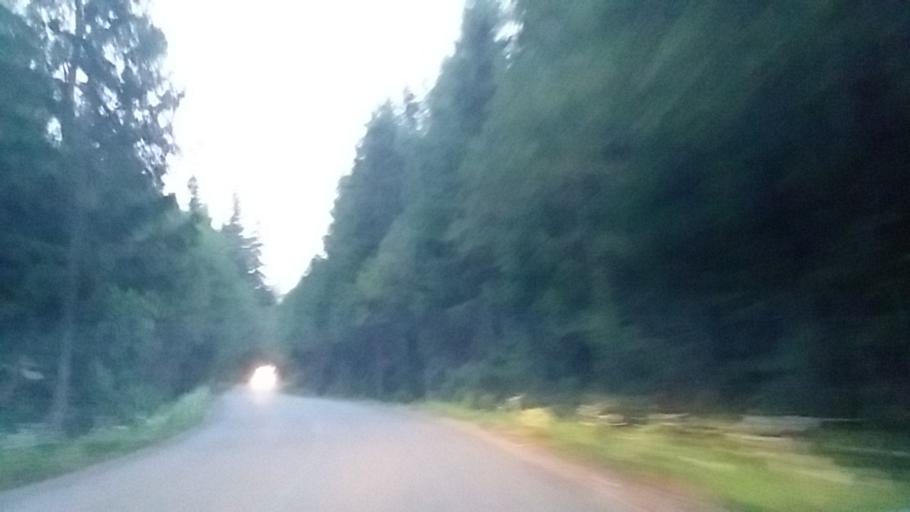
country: US
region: Washington
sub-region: Kittitas County
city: Cle Elum
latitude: 47.3544
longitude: -121.2532
